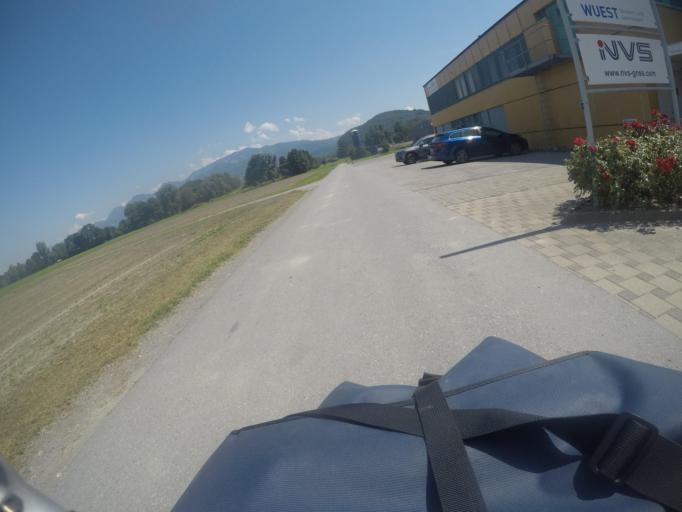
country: AT
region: Vorarlberg
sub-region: Politischer Bezirk Feldkirch
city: Koblach
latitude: 47.3491
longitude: 9.5939
